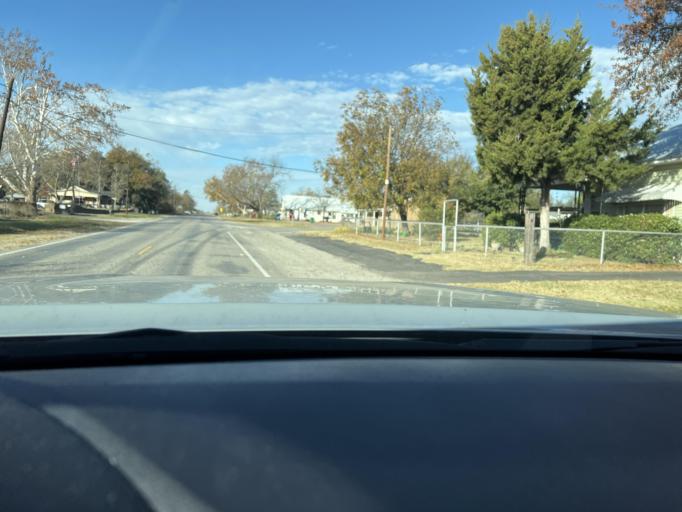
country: US
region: Texas
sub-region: Eastland County
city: Eastland
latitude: 32.4193
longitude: -98.7517
